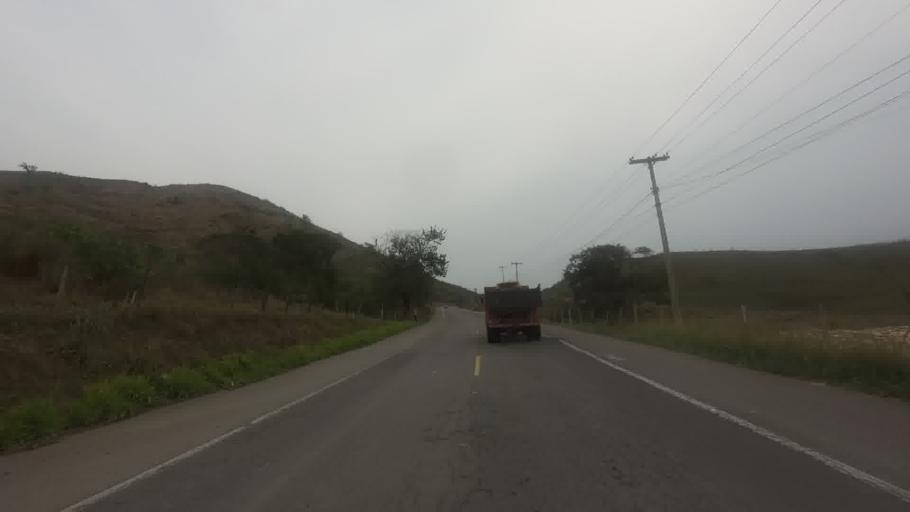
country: BR
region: Rio de Janeiro
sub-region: Santo Antonio De Padua
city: Santo Antonio de Padua
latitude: -21.5956
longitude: -42.2284
